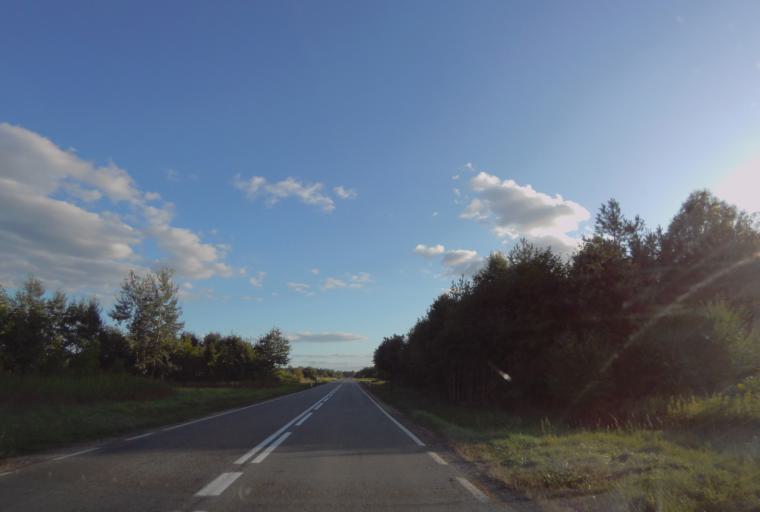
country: PL
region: Subcarpathian Voivodeship
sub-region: Powiat nizanski
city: Krzeszow
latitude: 50.3632
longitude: 22.3214
